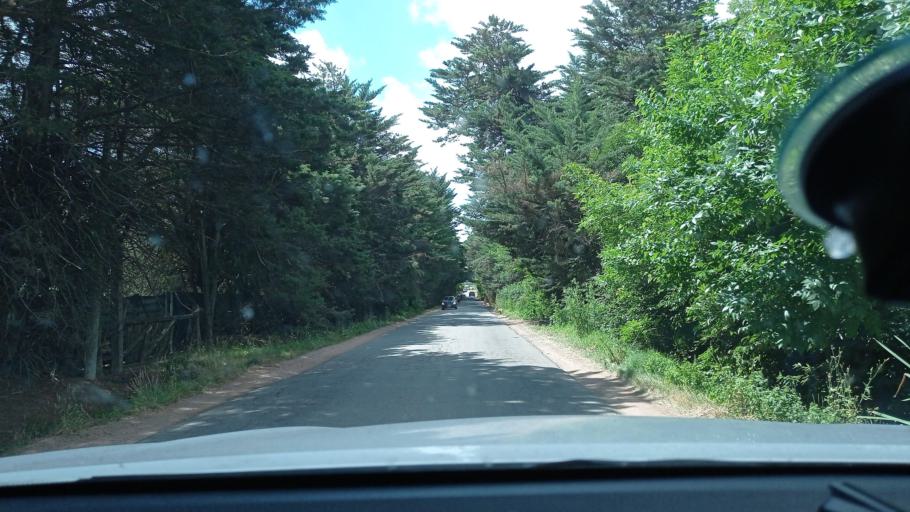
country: UY
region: Canelones
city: La Paz
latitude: -34.7985
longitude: -56.2107
